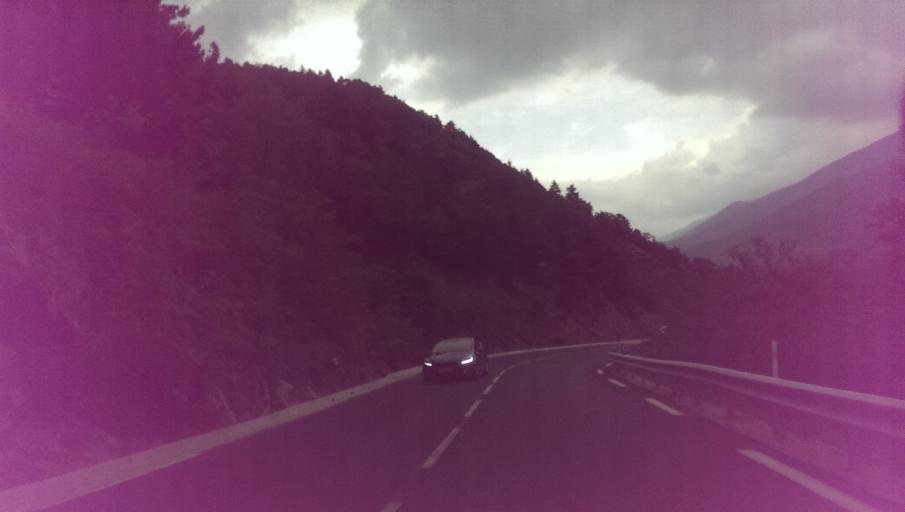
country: ES
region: Catalonia
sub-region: Provincia de Girona
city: Llivia
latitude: 42.5062
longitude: 2.1605
